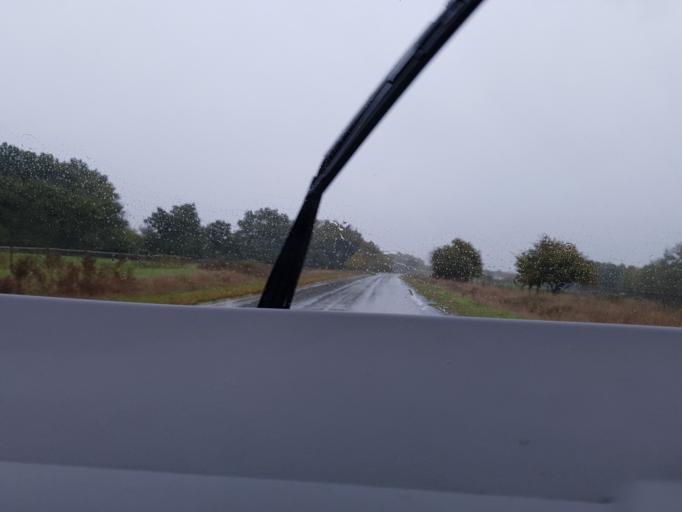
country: FR
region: Aquitaine
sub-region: Departement de la Gironde
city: Saint-Louis-de-Montferrand
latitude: 44.9607
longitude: -0.5142
